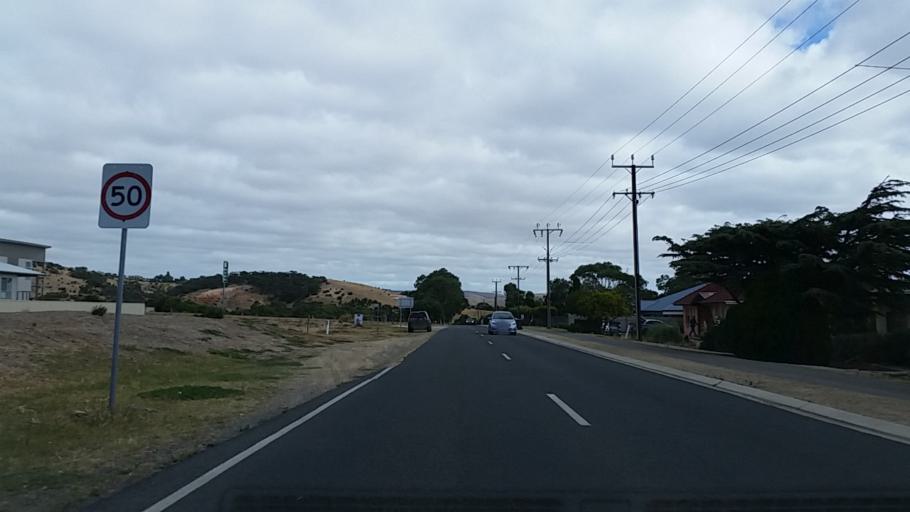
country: AU
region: South Australia
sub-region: Yankalilla
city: Normanville
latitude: -35.4276
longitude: 138.3269
